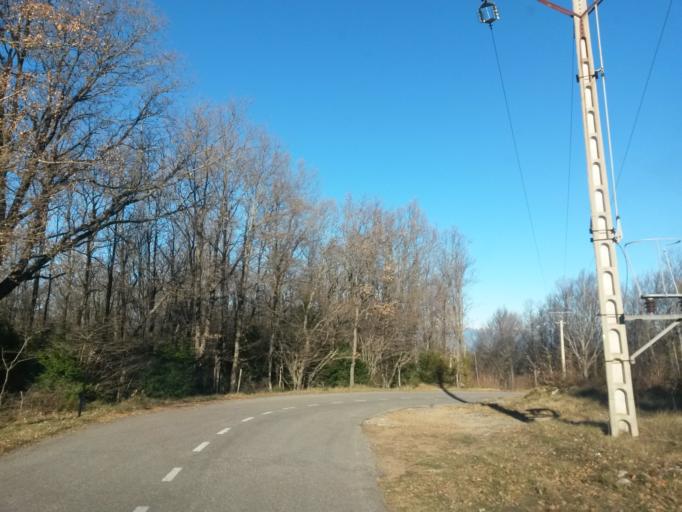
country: ES
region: Catalonia
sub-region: Provincia de Girona
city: les Planes d'Hostoles
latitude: 42.0236
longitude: 2.5351
